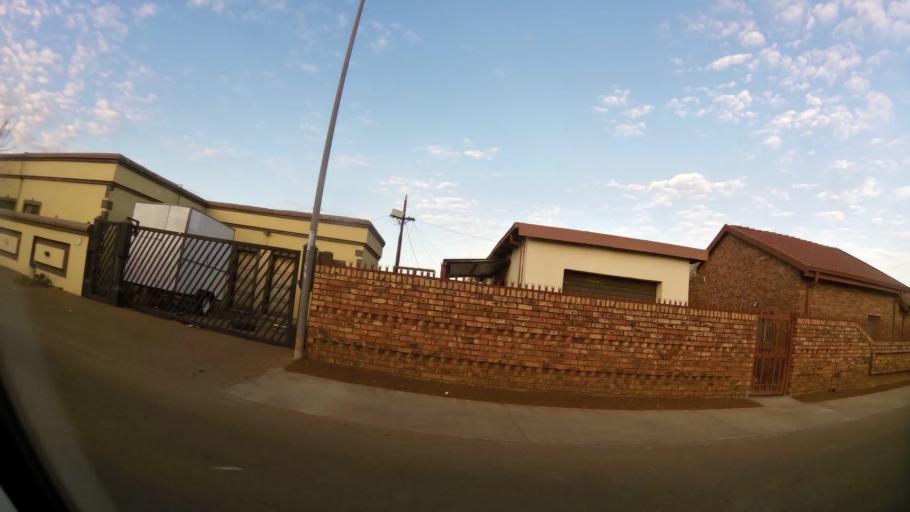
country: ZA
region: Gauteng
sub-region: City of Tshwane Metropolitan Municipality
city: Pretoria
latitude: -25.7151
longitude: 28.3490
